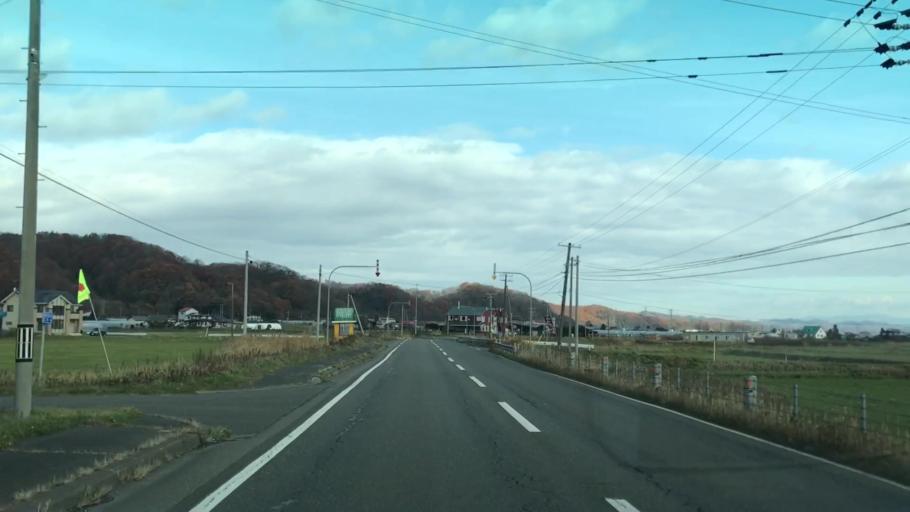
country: JP
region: Hokkaido
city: Shizunai-furukawacho
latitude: 42.5424
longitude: 142.0577
